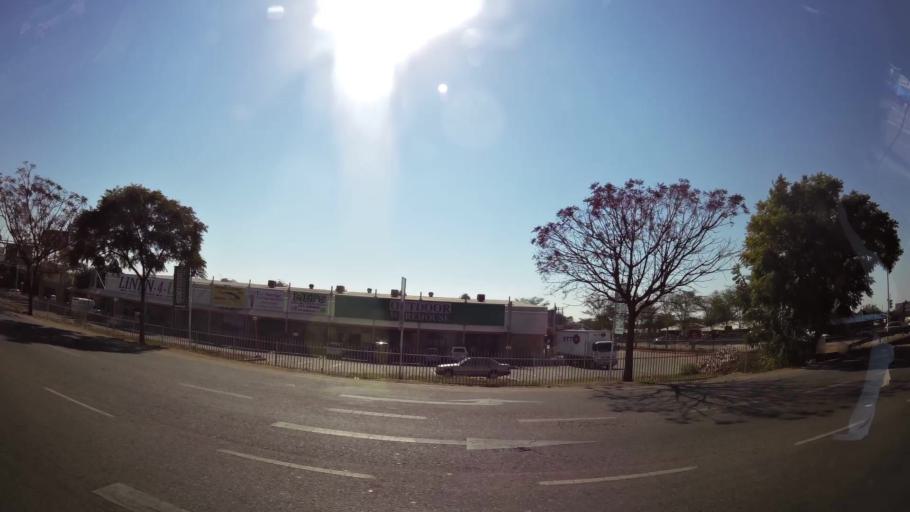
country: ZA
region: Gauteng
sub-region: City of Tshwane Metropolitan Municipality
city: Pretoria
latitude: -25.6830
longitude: 28.2751
